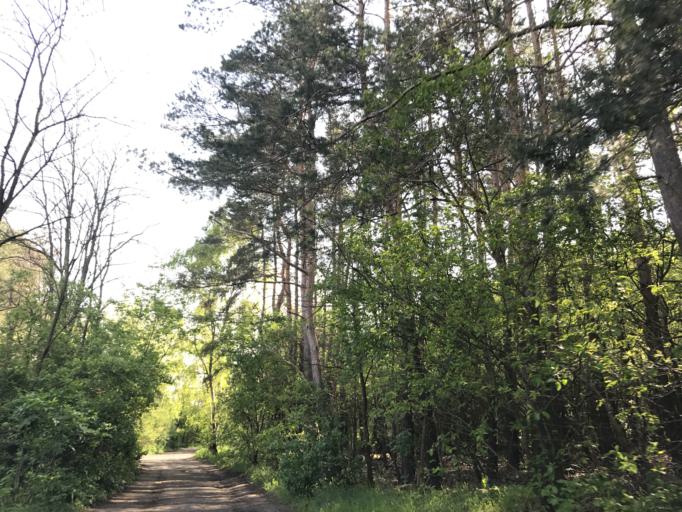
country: DE
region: Berlin
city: Staaken
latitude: 52.5251
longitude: 13.1241
